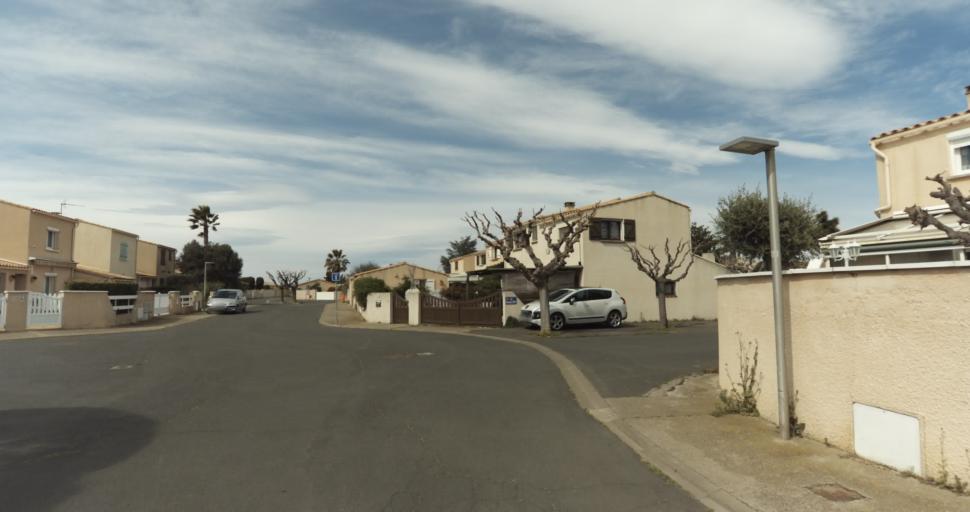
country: FR
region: Languedoc-Roussillon
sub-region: Departement de l'Herault
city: Marseillan
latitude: 43.3429
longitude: 3.5297
